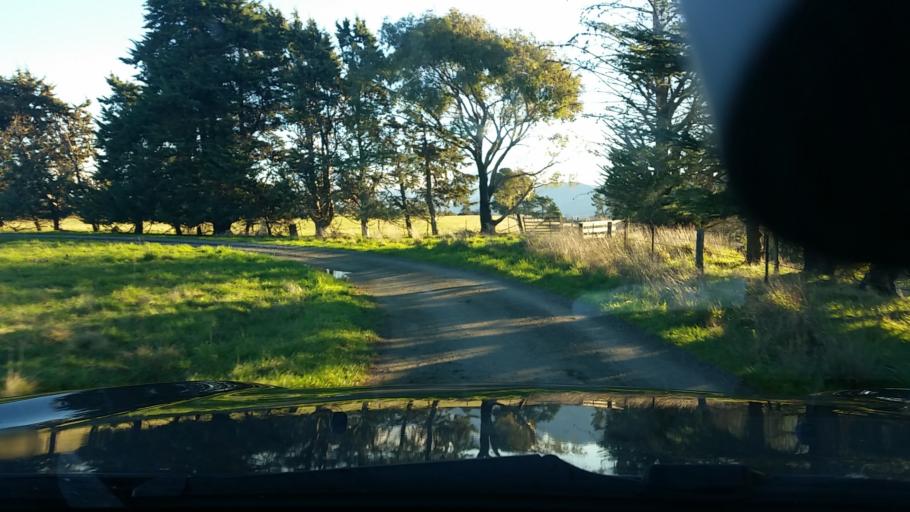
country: NZ
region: Marlborough
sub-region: Marlborough District
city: Blenheim
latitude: -41.6696
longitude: 174.0391
